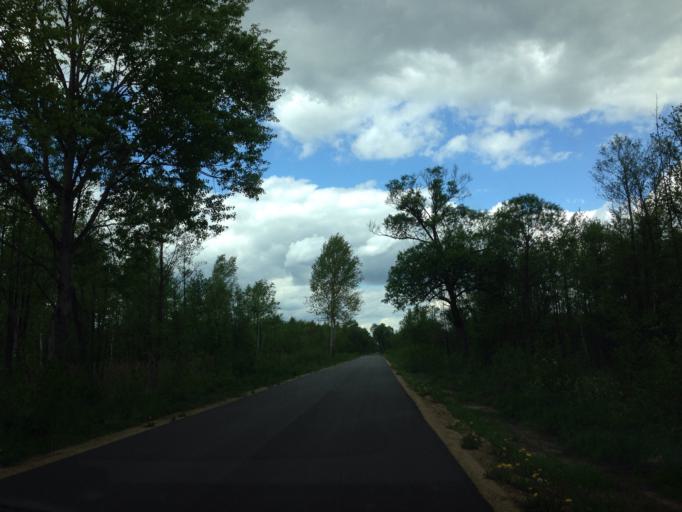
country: PL
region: Podlasie
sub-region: Powiat bialostocki
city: Tykocin
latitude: 53.3079
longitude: 22.6036
